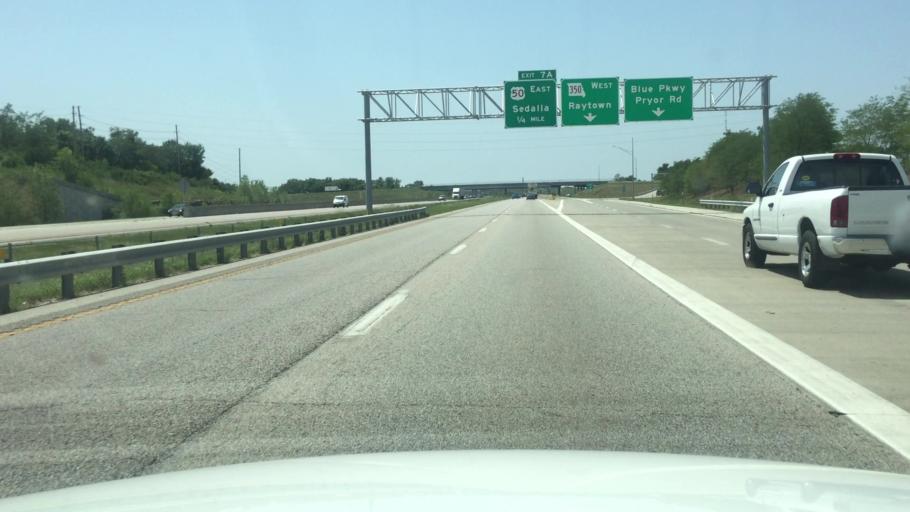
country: US
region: Missouri
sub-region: Jackson County
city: Lees Summit
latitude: 38.9385
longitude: -94.3977
